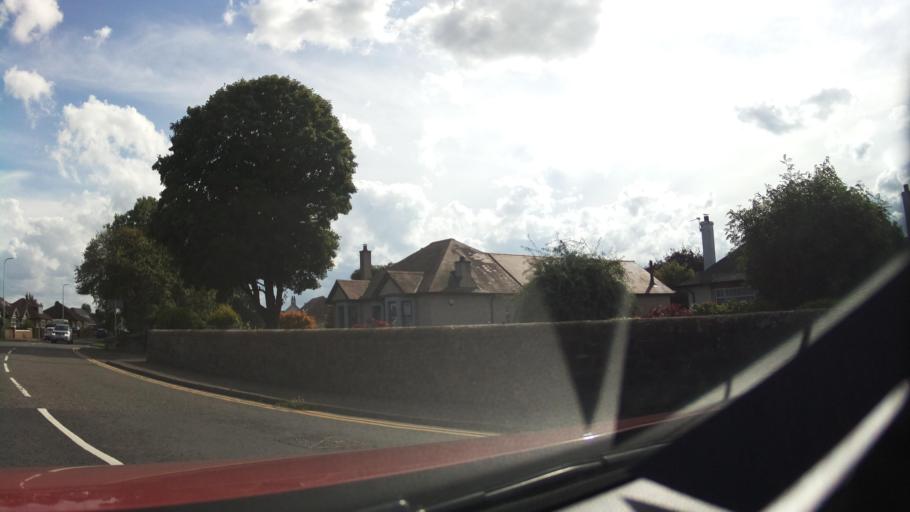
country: GB
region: Scotland
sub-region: Falkirk
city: Larbert
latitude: 56.0242
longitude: -3.8376
